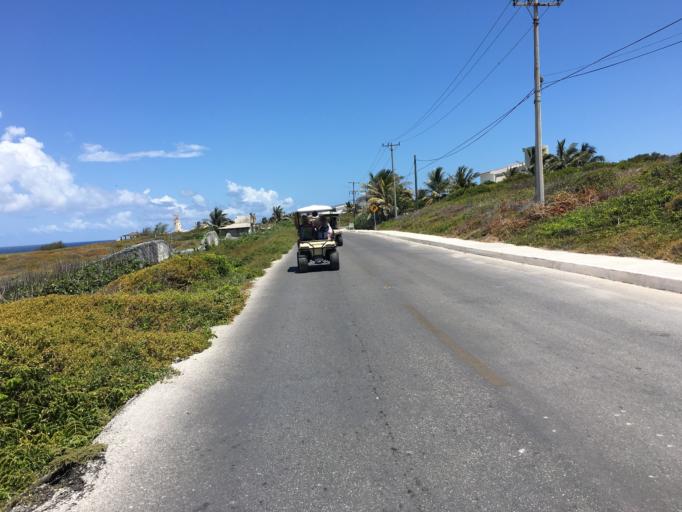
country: MX
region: Quintana Roo
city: Isla Mujeres
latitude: 21.2063
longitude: -86.7155
